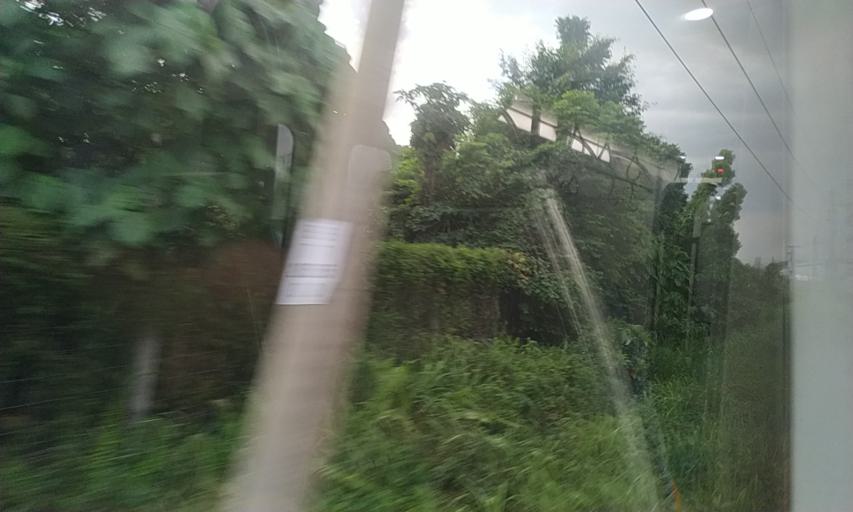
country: MY
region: Kuala Lumpur
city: Kuala Lumpur
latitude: 3.2282
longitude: 101.6729
